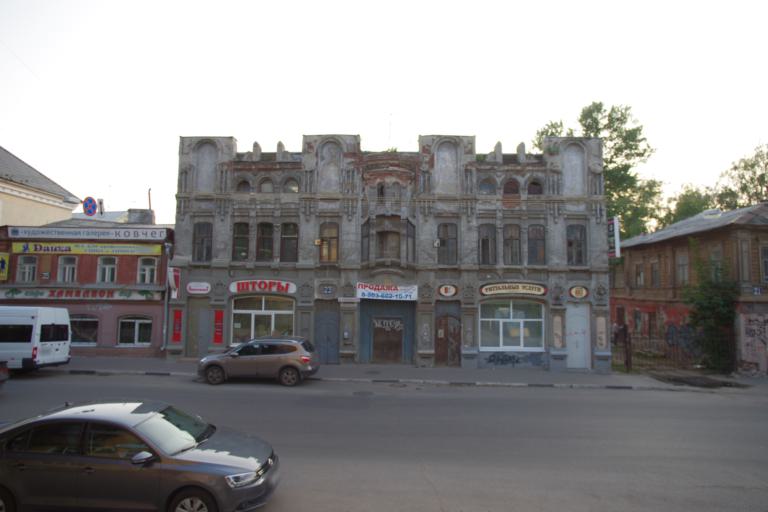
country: RU
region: Nizjnij Novgorod
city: Nizhniy Novgorod
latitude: 56.3213
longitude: 44.0041
